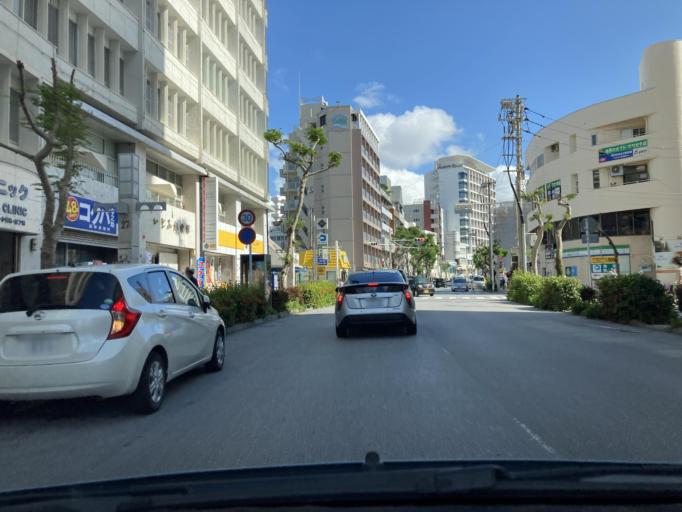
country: JP
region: Okinawa
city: Naha-shi
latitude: 26.2188
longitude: 127.6860
